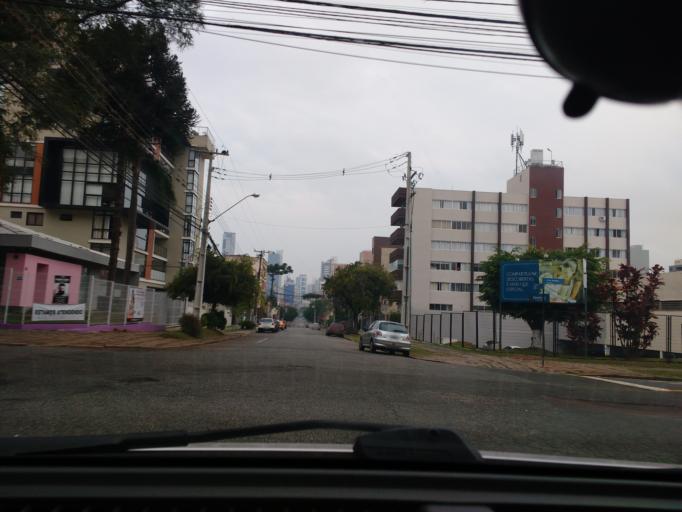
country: BR
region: Parana
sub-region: Curitiba
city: Curitiba
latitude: -25.4268
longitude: -49.2840
